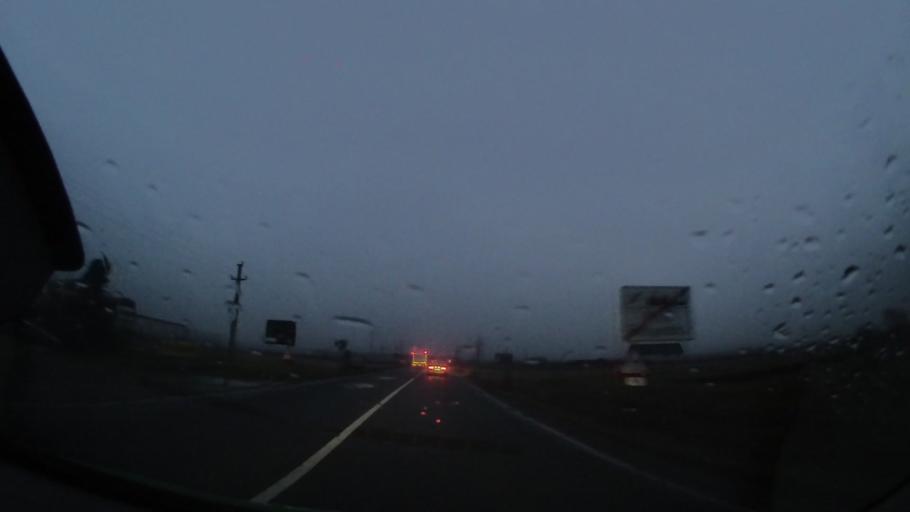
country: RO
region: Harghita
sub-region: Comuna Ditrau
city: Ditrau
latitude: 46.8147
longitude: 25.4929
